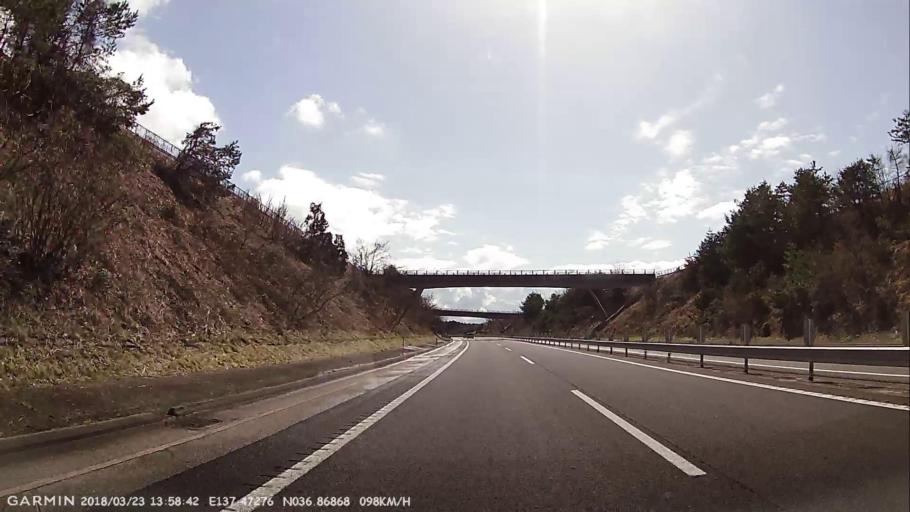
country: JP
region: Toyama
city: Nyuzen
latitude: 36.8683
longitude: 137.4724
